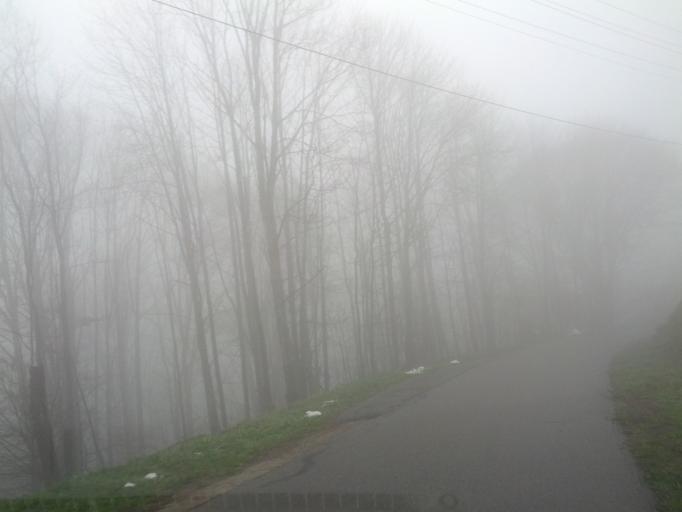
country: DE
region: Baden-Wuerttemberg
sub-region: Freiburg Region
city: Wieden
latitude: 47.8421
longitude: 7.8693
